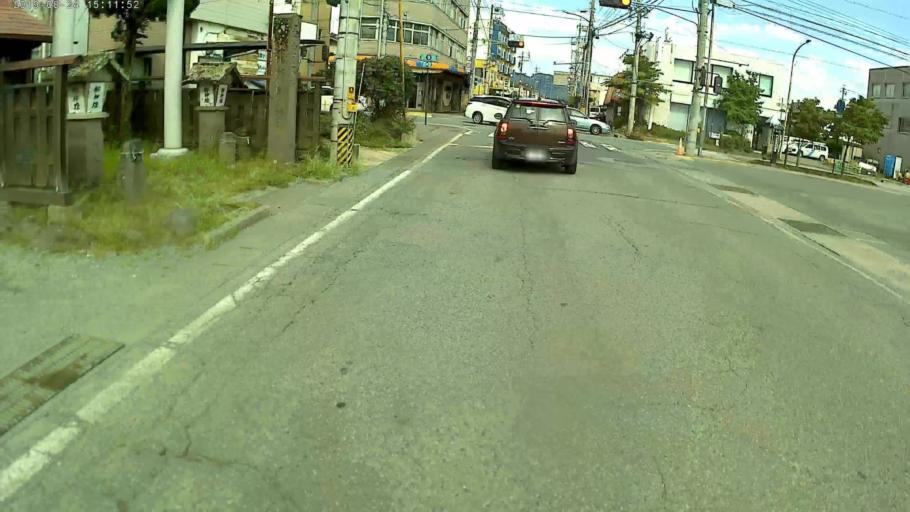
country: JP
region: Nagano
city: Saku
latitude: 36.2709
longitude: 138.4779
